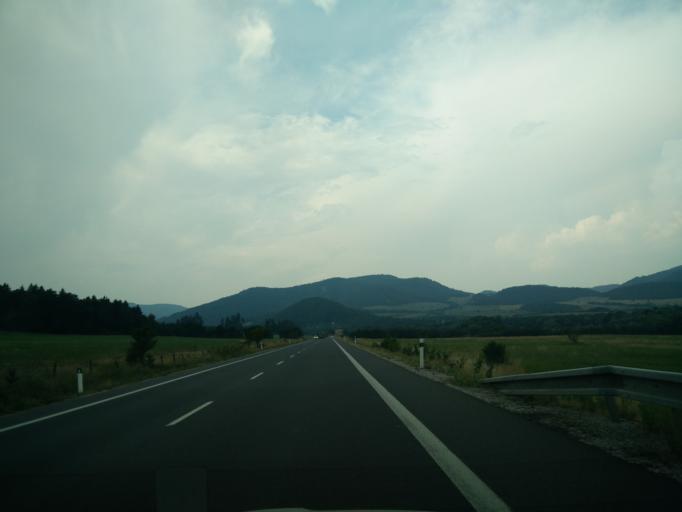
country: SK
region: Banskobystricky
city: Ziar nad Hronom
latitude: 48.6374
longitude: 18.7746
